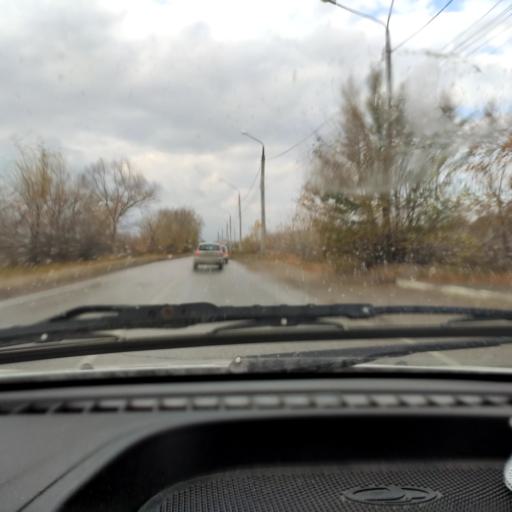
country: RU
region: Samara
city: Zhigulevsk
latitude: 53.4638
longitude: 49.5554
